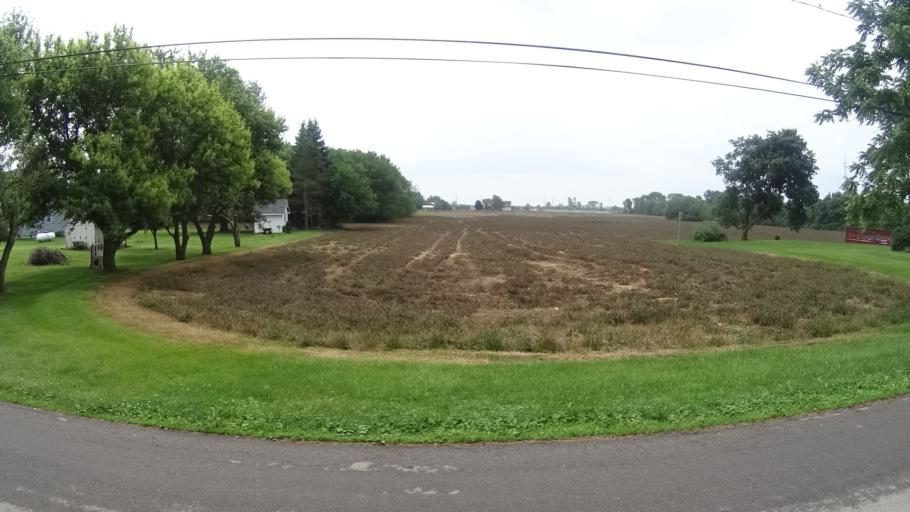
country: US
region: Ohio
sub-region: Huron County
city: Bellevue
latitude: 41.3496
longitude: -82.7720
